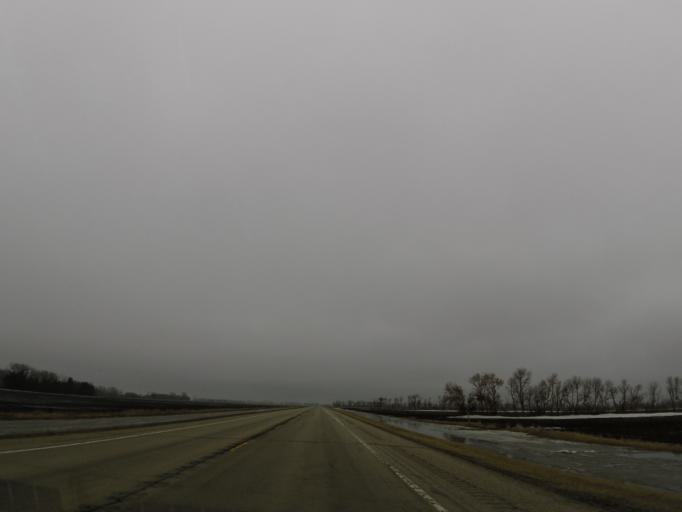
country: US
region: North Dakota
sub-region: Walsh County
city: Grafton
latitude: 48.5200
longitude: -97.4478
